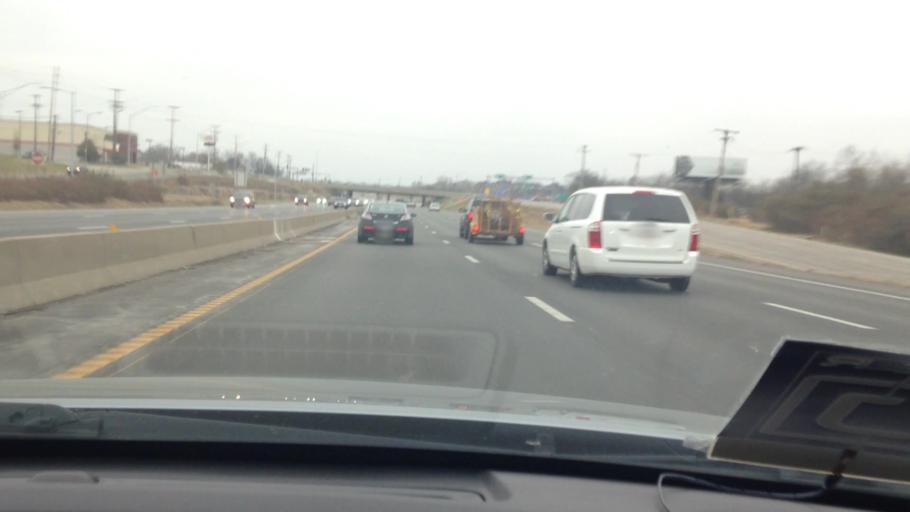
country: US
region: Missouri
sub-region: Jackson County
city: Grandview
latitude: 38.9042
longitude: -94.5241
